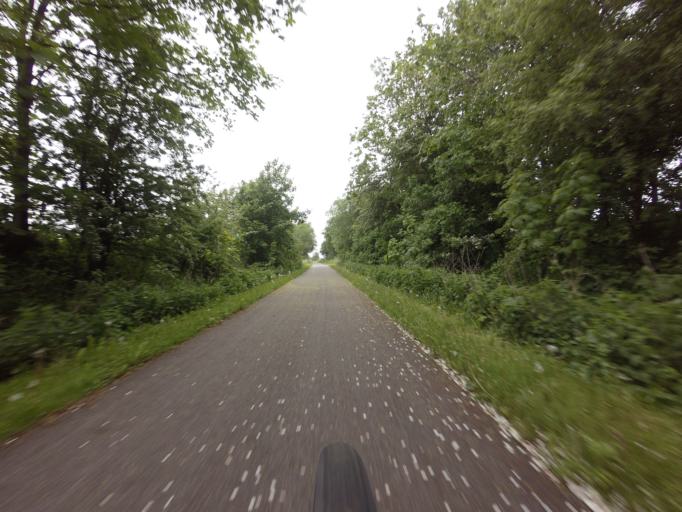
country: DK
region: Zealand
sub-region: Slagelse Kommune
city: Skaelskor
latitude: 55.2744
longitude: 11.4190
